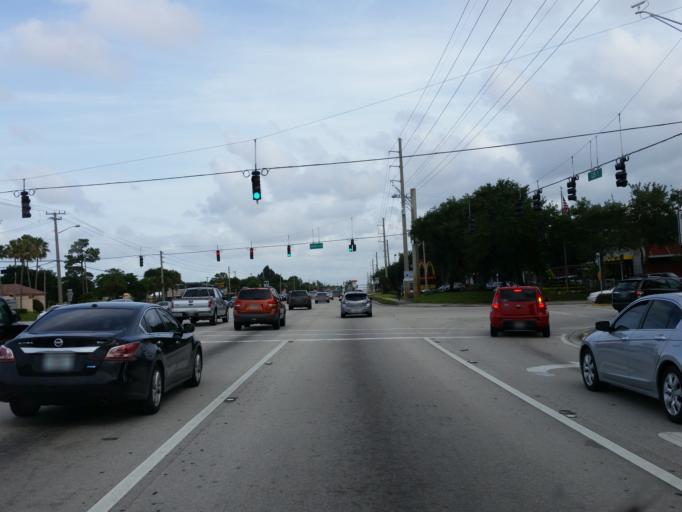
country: US
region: Florida
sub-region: Martin County
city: North River Shores
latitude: 27.2460
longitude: -80.2727
